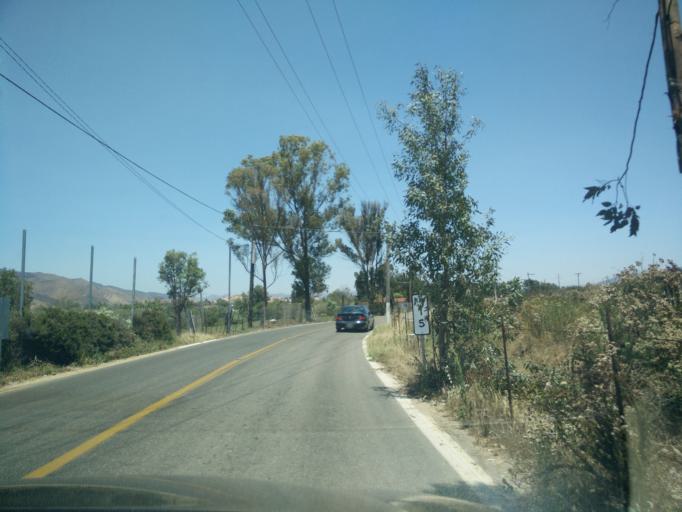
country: MX
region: Baja California
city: El Sauzal
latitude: 32.0087
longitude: -116.6793
